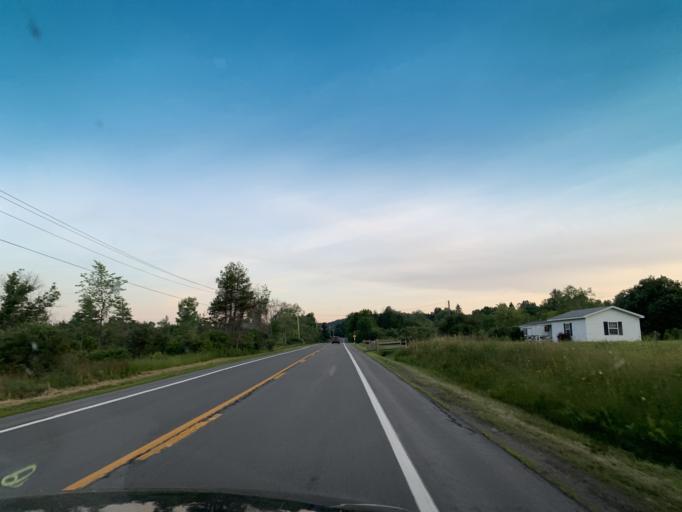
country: US
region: New York
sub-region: Oneida County
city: Waterville
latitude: 42.8889
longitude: -75.2482
